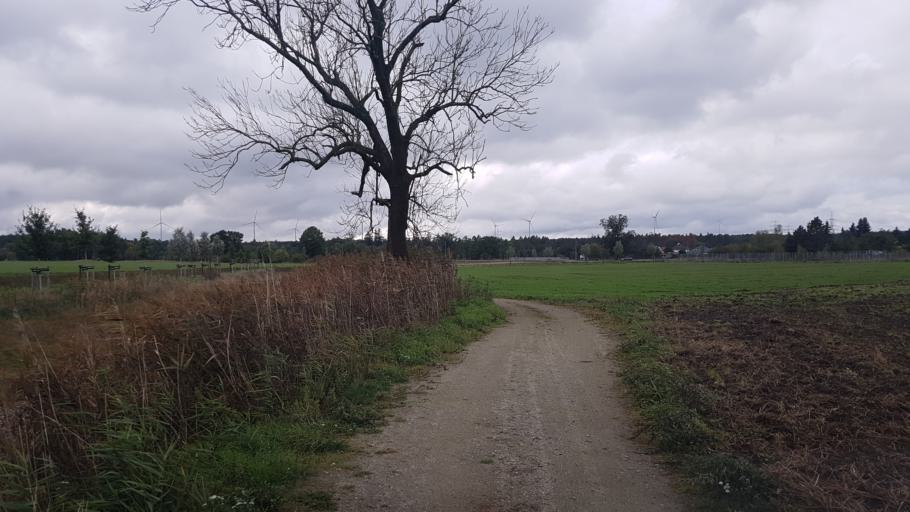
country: DE
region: Brandenburg
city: Altdobern
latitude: 51.6461
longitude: 14.0298
